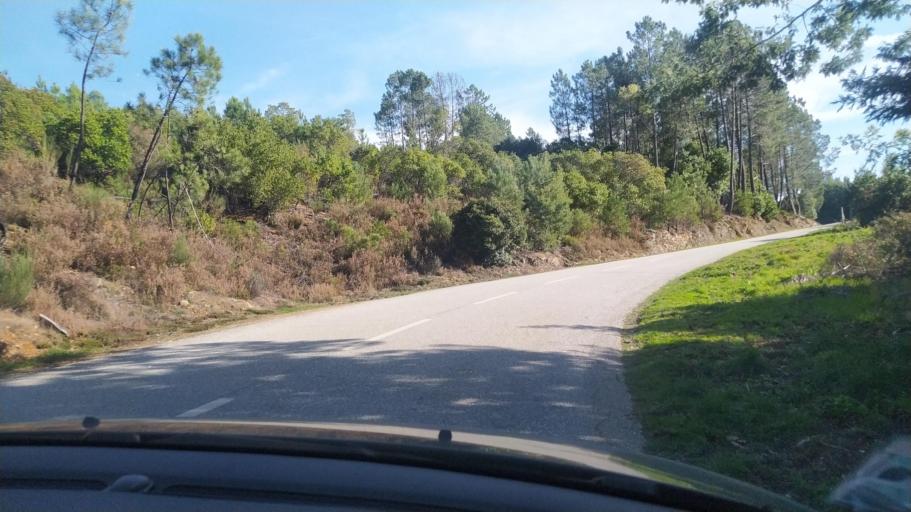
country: PT
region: Coimbra
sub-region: Oliveira do Hospital
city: Oliveira do Hospital
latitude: 40.2025
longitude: -7.7370
